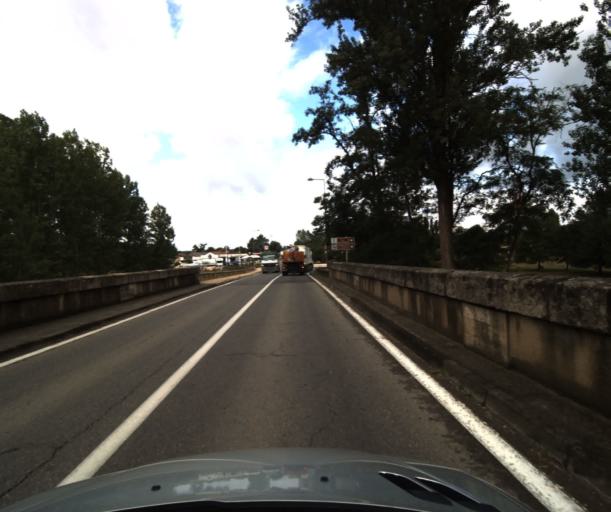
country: FR
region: Midi-Pyrenees
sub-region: Departement du Tarn-et-Garonne
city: Saint-Nicolas-de-la-Grave
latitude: 44.0305
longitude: 1.0394
